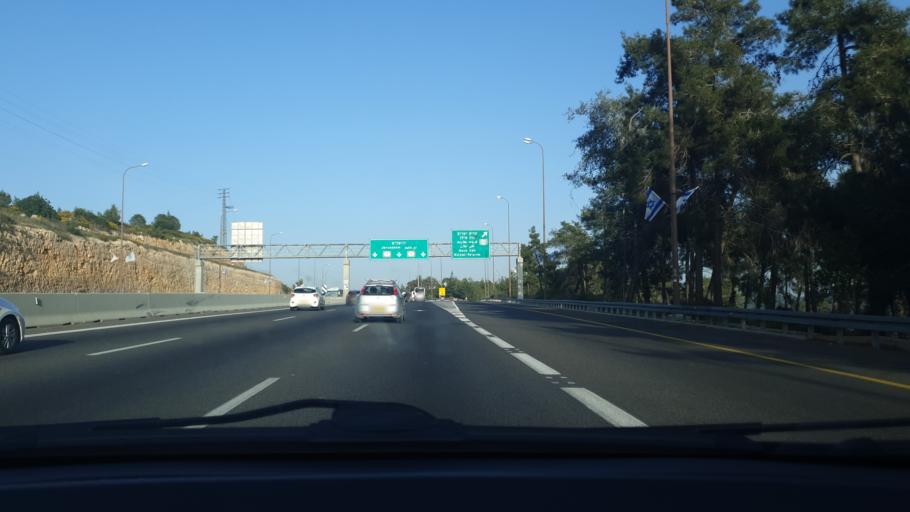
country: IL
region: Jerusalem
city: Abu Ghaush
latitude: 31.8006
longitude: 35.0835
